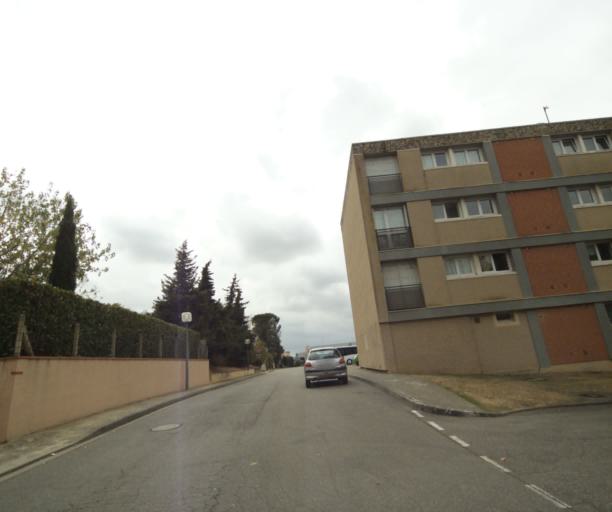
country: FR
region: Midi-Pyrenees
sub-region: Departement de la Haute-Garonne
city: Villefranche-de-Lauragais
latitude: 43.4024
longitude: 1.7209
